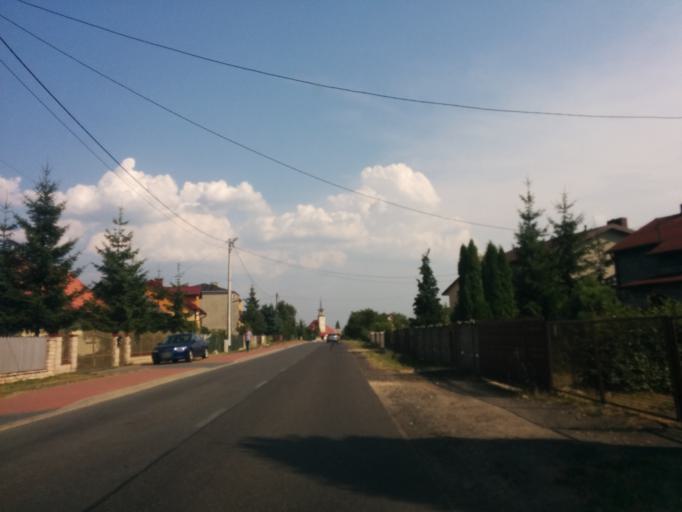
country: PL
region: Silesian Voivodeship
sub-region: Powiat myszkowski
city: Choron
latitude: 50.7062
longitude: 19.2825
